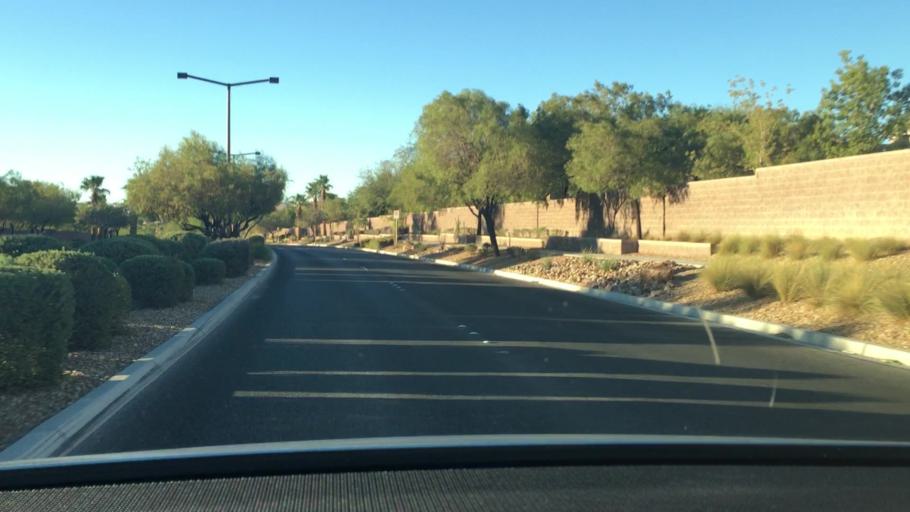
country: US
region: Nevada
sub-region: Clark County
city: Summerlin South
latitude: 36.1320
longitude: -115.3430
